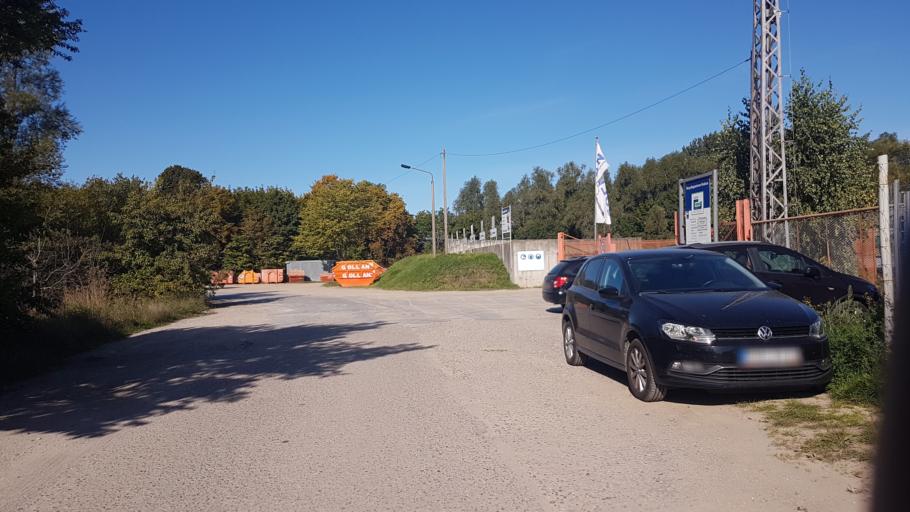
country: DE
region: Mecklenburg-Vorpommern
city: Sagard
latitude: 54.5014
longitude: 13.5368
